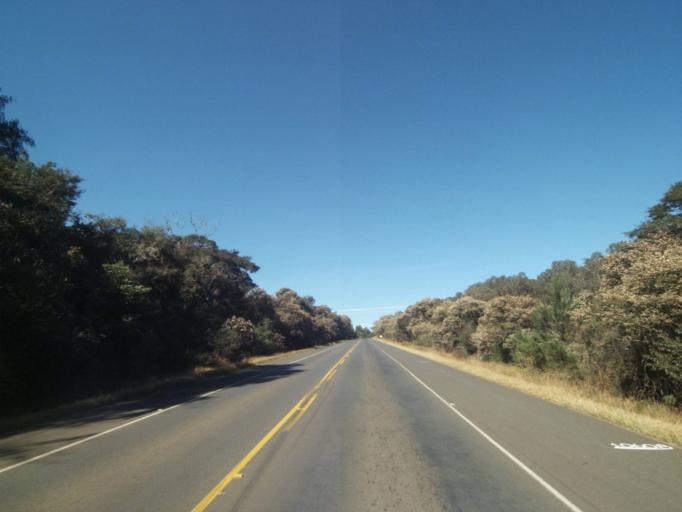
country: BR
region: Parana
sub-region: Tibagi
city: Tibagi
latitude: -24.5550
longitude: -50.4563
